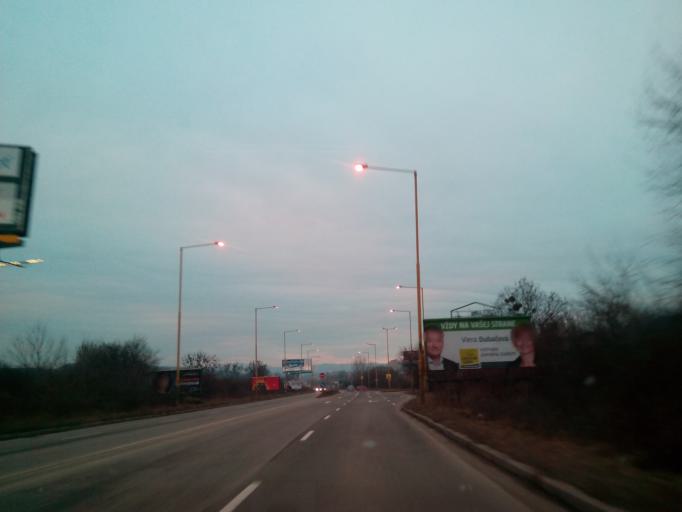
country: SK
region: Kosicky
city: Kosice
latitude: 48.6973
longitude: 21.2278
